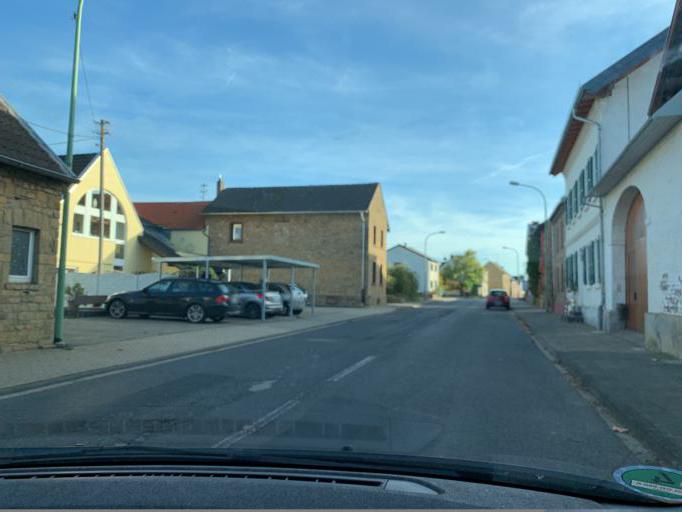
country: DE
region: North Rhine-Westphalia
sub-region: Regierungsbezirk Koln
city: Nideggen
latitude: 50.7076
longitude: 6.5194
